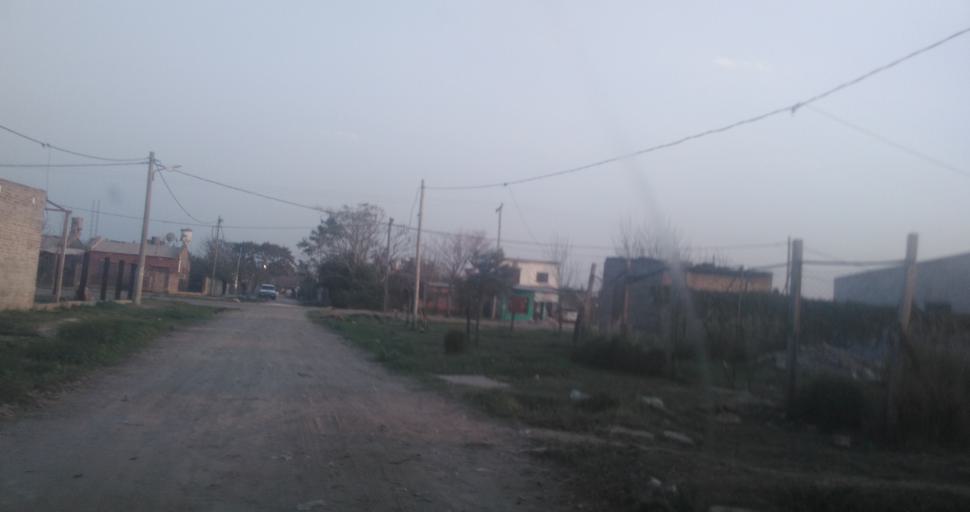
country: AR
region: Chaco
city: Resistencia
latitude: -27.4663
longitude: -59.0169
